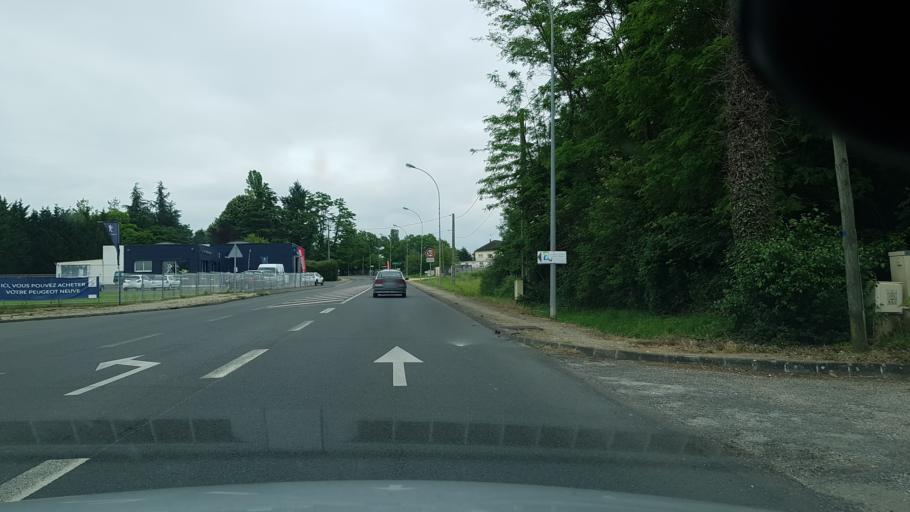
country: FR
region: Centre
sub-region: Departement du Loir-et-Cher
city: Selles-sur-Cher
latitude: 47.2849
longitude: 1.5388
